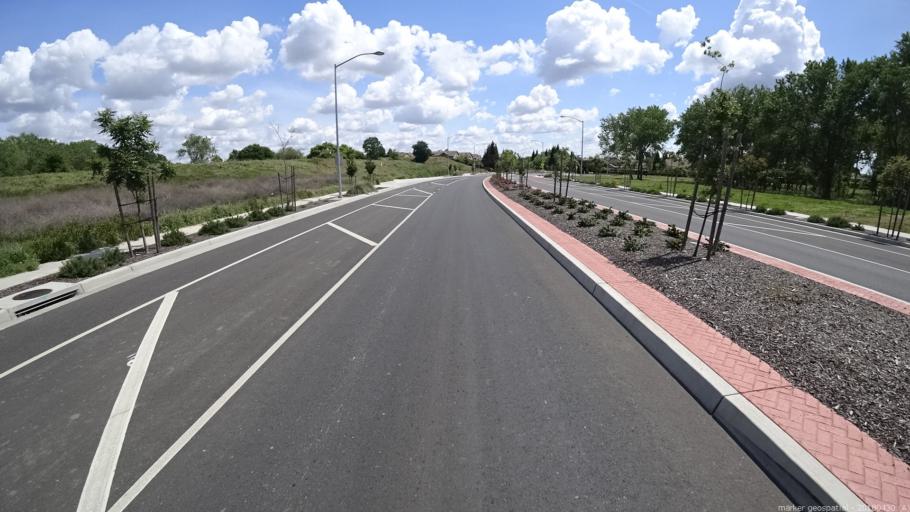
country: US
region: California
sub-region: Yolo County
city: West Sacramento
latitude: 38.5558
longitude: -121.5220
